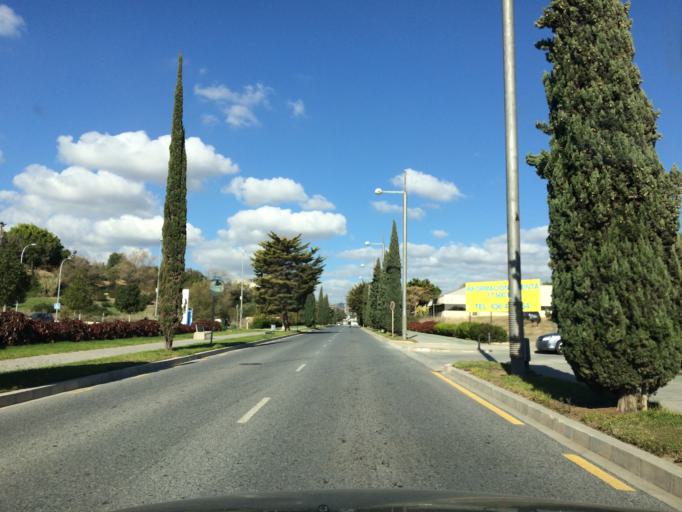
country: ES
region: Andalusia
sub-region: Provincia de Malaga
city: Estacion de Cartama
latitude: 36.7335
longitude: -4.5510
